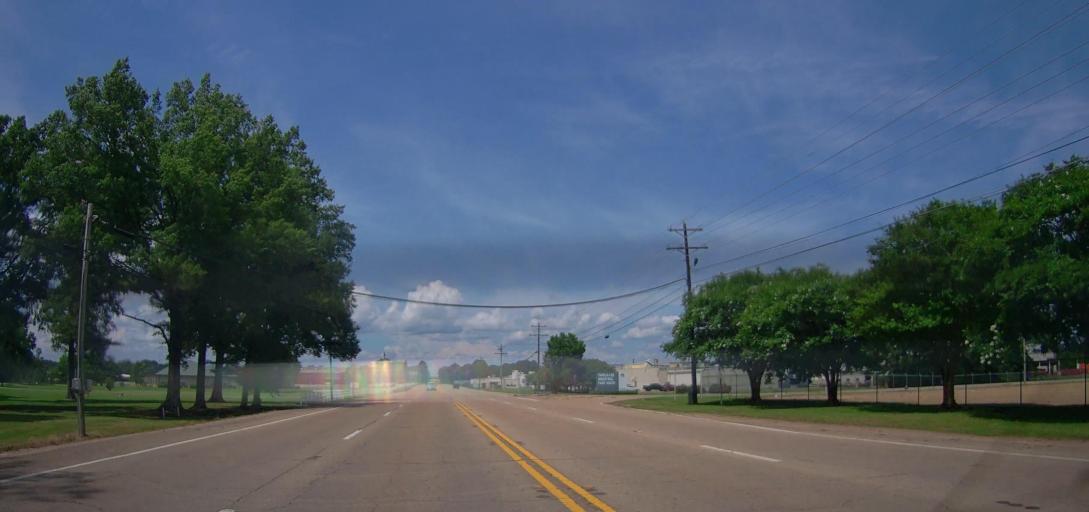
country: US
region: Mississippi
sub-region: Lee County
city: Verona
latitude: 34.1630
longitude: -88.7195
